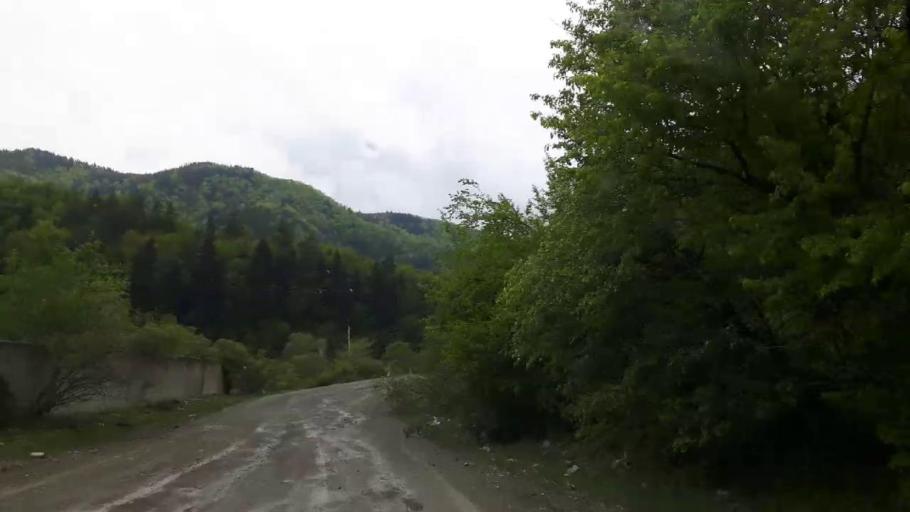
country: GE
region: Shida Kartli
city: Gori
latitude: 41.8702
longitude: 43.9853
